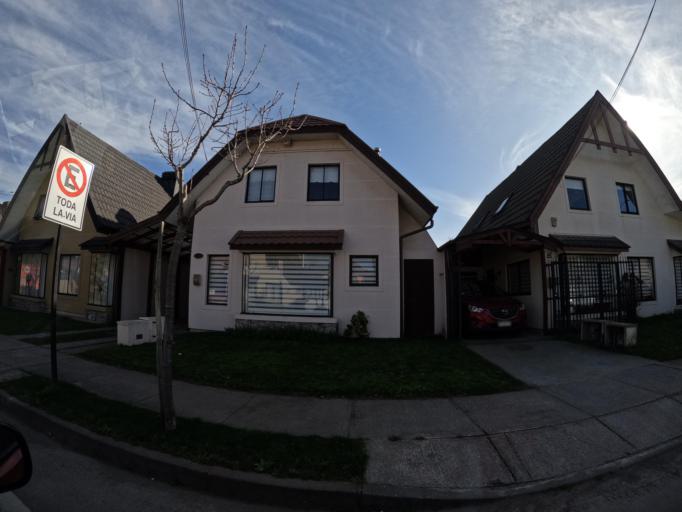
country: CL
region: Biobio
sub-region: Provincia de Concepcion
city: Talcahuano
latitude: -36.7704
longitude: -73.0772
